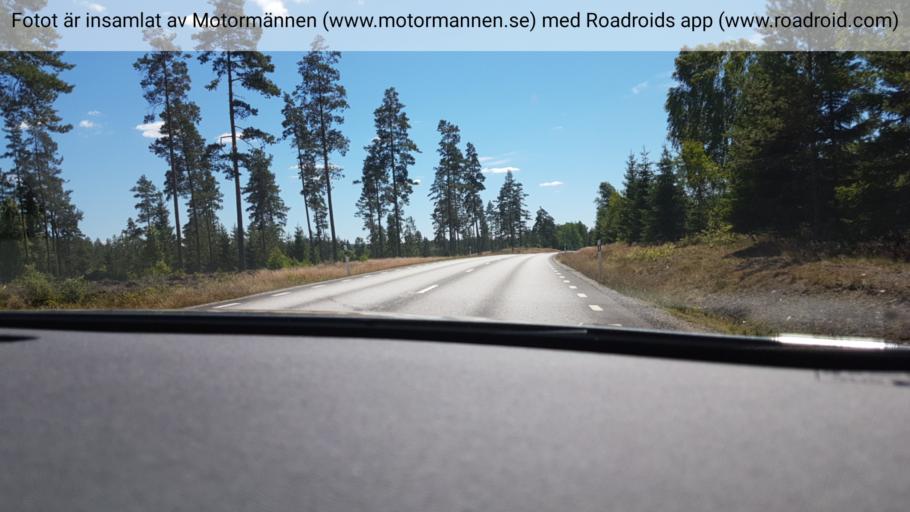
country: SE
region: Joenkoeping
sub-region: Gnosjo Kommun
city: Gnosjoe
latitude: 57.5274
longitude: 13.6855
